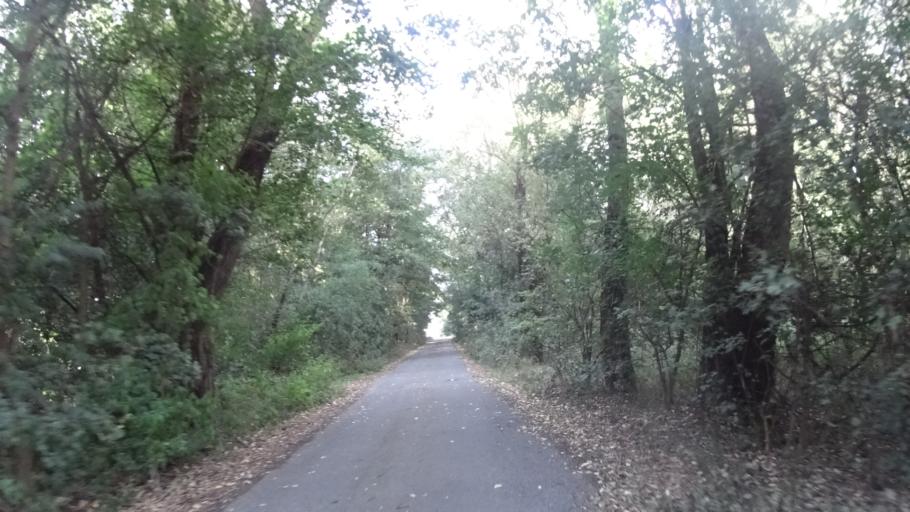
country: AT
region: Lower Austria
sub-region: Politischer Bezirk Mistelbach
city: Rabensburg
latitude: 48.5984
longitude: 16.9499
